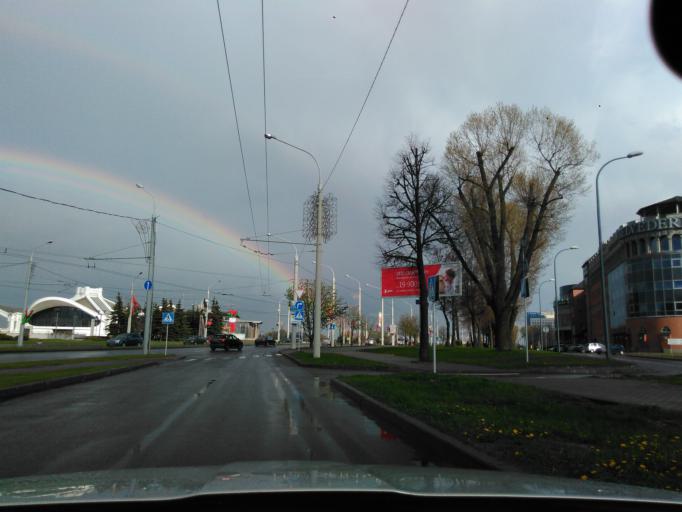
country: BY
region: Minsk
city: Minsk
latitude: 53.9280
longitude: 27.5160
